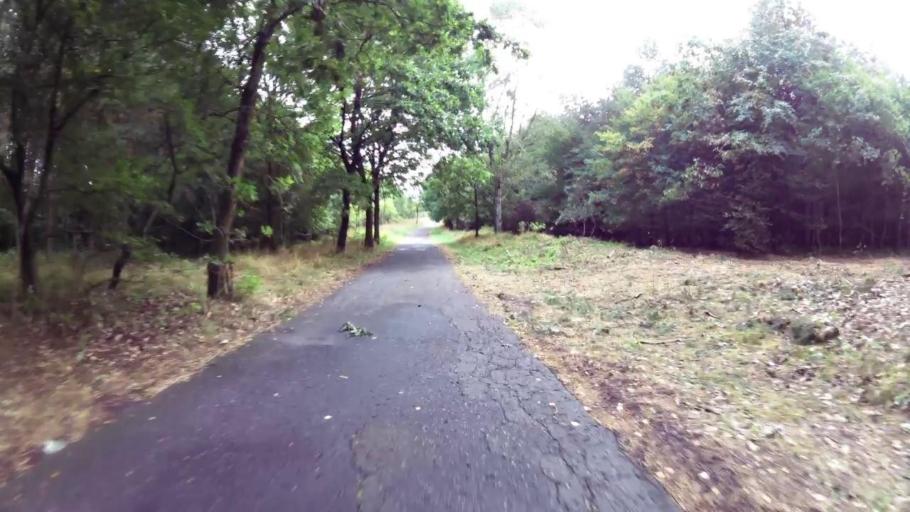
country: PL
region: West Pomeranian Voivodeship
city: Trzcinsko Zdroj
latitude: 52.8905
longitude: 14.7078
